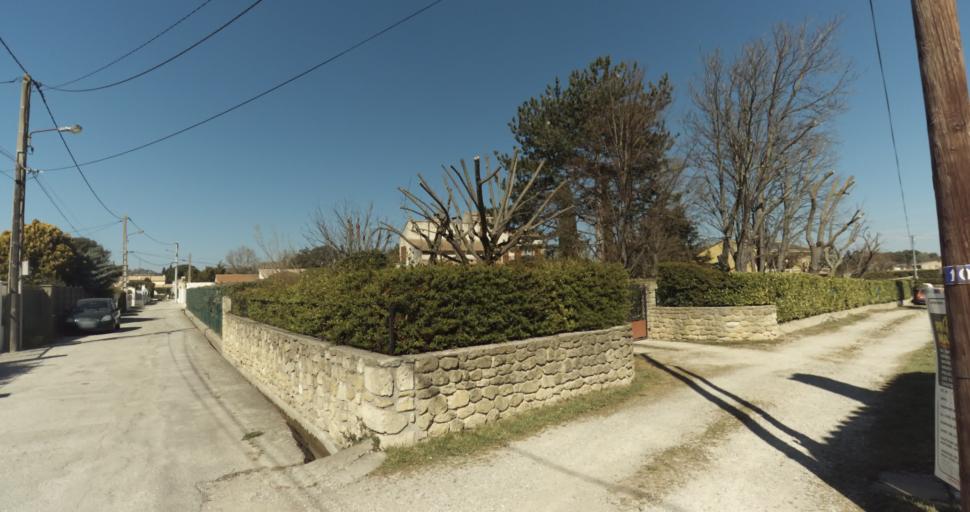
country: FR
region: Provence-Alpes-Cote d'Azur
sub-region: Departement des Bouches-du-Rhone
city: Pelissanne
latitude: 43.6339
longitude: 5.1544
